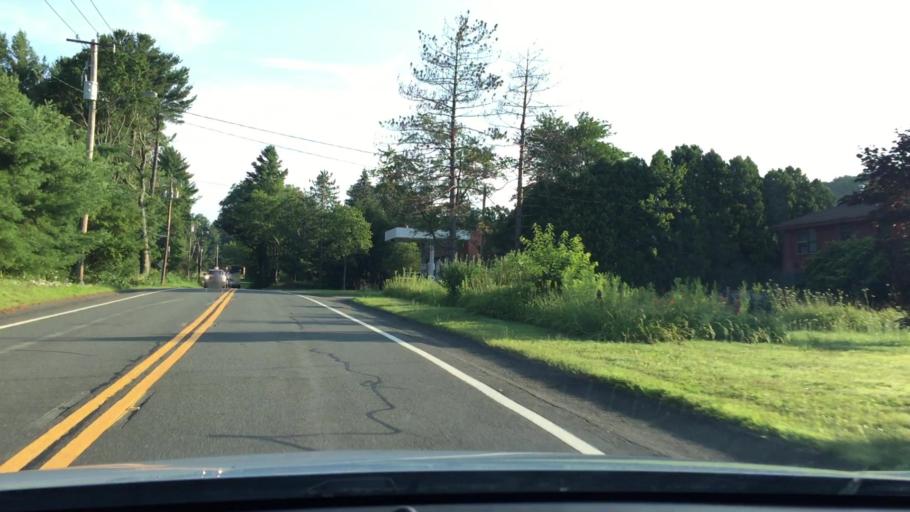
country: US
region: Massachusetts
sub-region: Berkshire County
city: Otis
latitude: 42.1999
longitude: -73.0938
